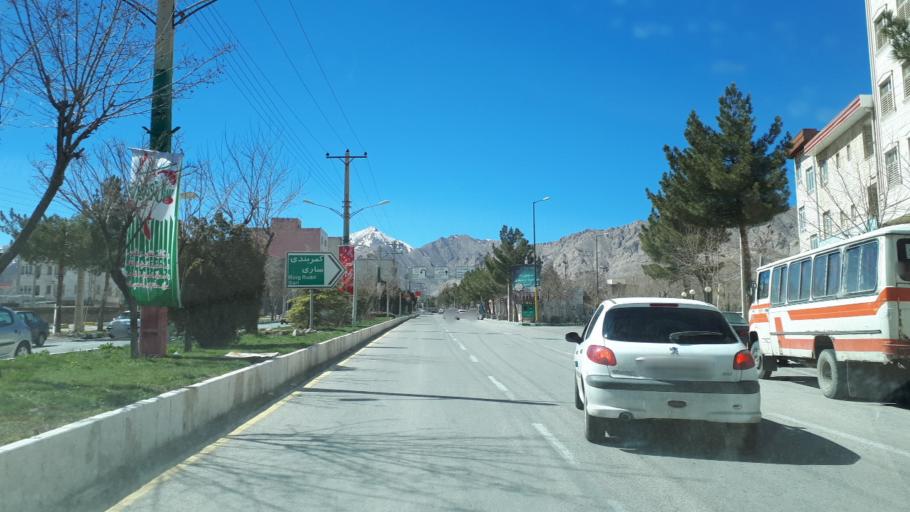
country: IR
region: Semnan
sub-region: Mahdishahr
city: Mahdishahr
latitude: 35.7622
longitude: 53.3526
